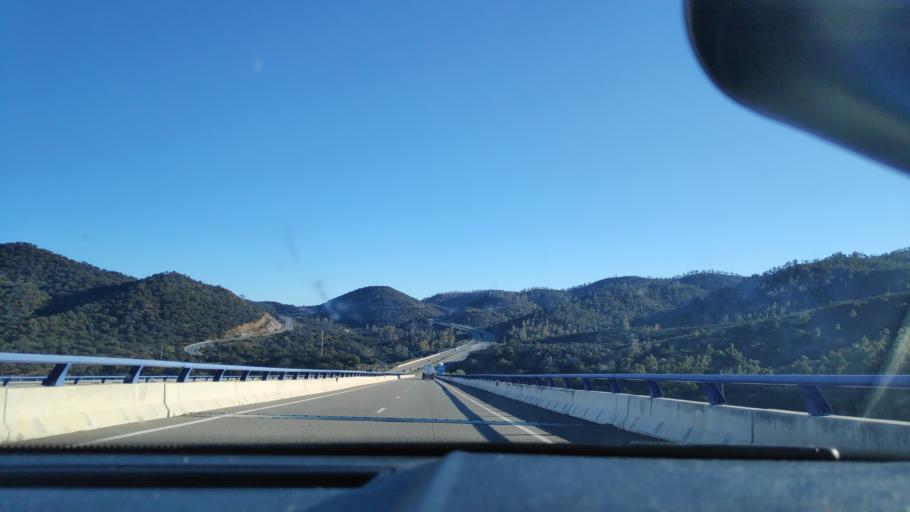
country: ES
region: Andalusia
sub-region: Provincia de Sevilla
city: El Ronquillo
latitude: 37.6741
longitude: -6.1740
